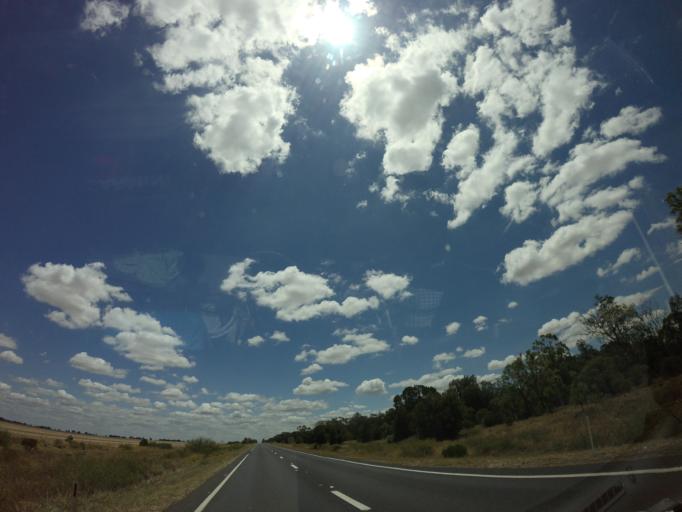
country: AU
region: New South Wales
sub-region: Moree Plains
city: Boggabilla
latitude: -28.8242
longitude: 150.2333
